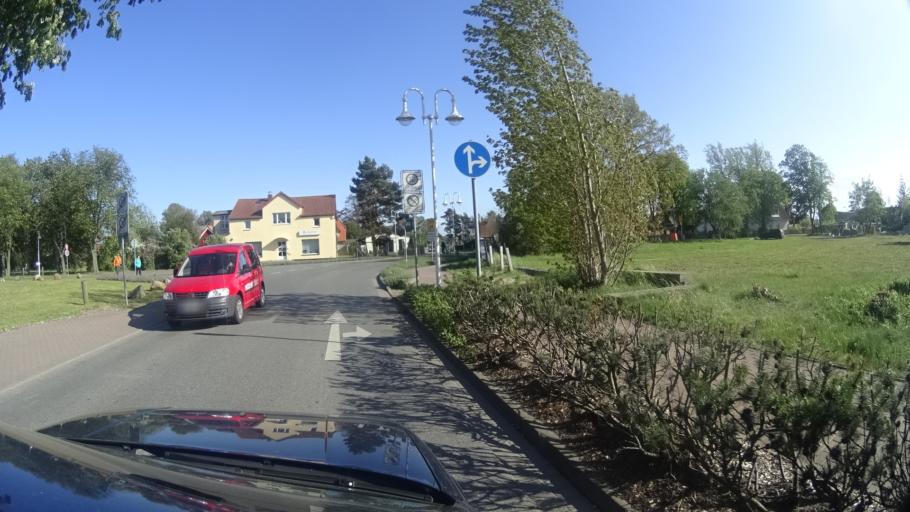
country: DE
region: Mecklenburg-Vorpommern
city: Ostseebad Prerow
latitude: 54.4435
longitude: 12.5779
